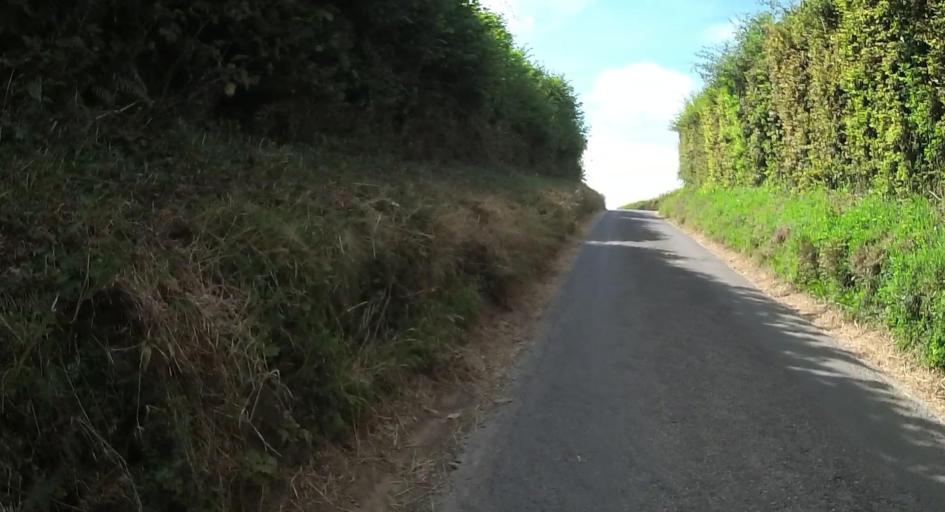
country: GB
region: England
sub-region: Dorset
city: Swanage
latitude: 50.6258
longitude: -1.9920
